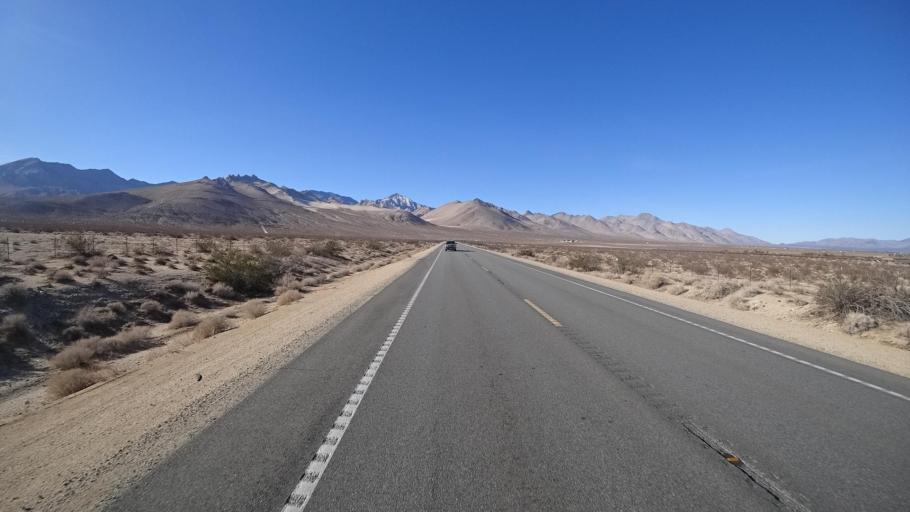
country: US
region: California
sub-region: Kern County
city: Inyokern
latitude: 35.6873
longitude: -117.8538
